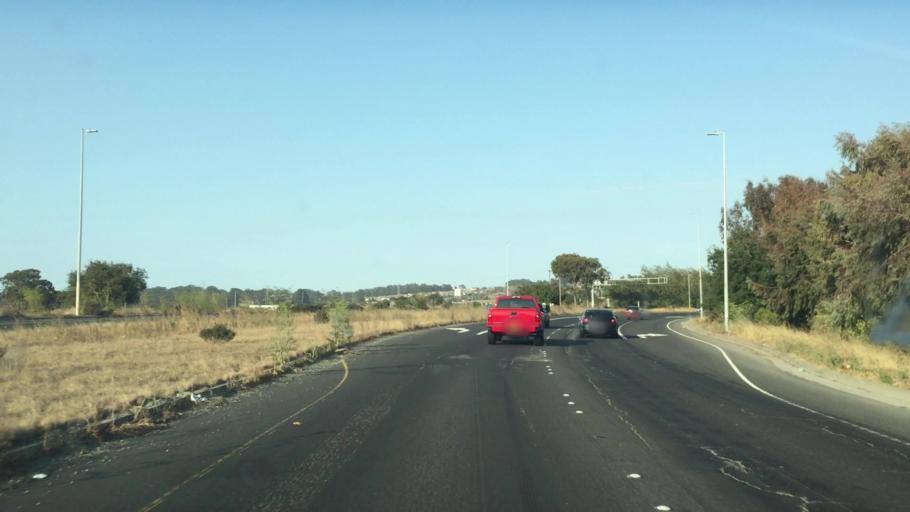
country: US
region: California
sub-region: Contra Costa County
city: North Richmond
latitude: 37.9739
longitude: -122.3677
